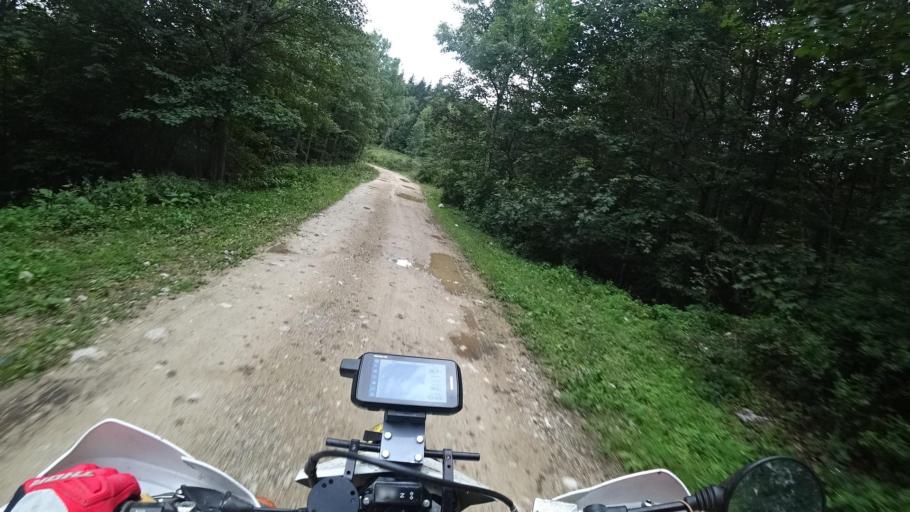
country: BA
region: Republika Srpska
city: Podbrdo
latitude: 44.5921
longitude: 17.0797
